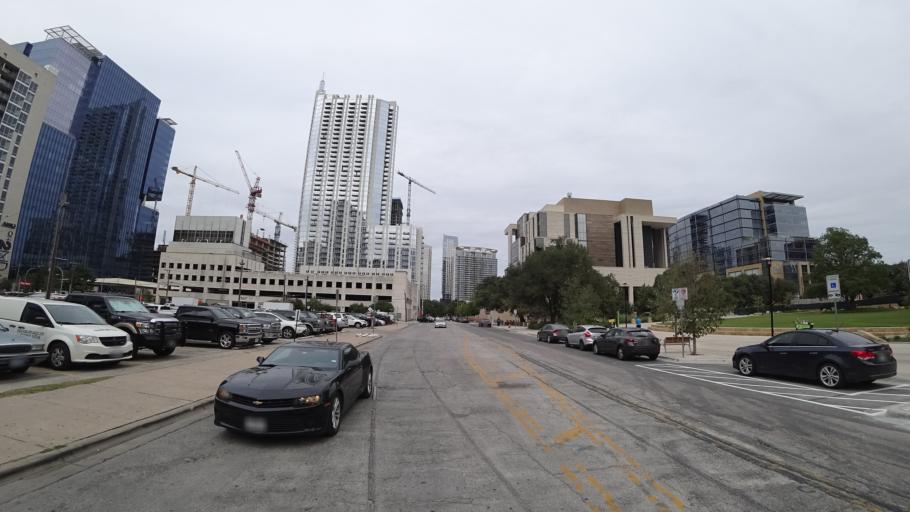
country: US
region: Texas
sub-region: Travis County
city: Austin
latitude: 30.2672
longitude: -97.7472
